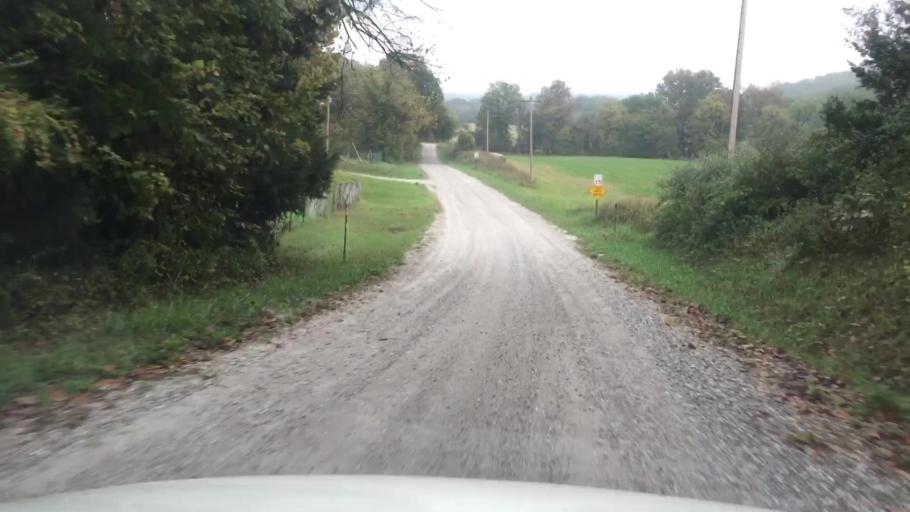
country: US
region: Missouri
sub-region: Boone County
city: Ashland
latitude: 38.8203
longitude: -92.3464
